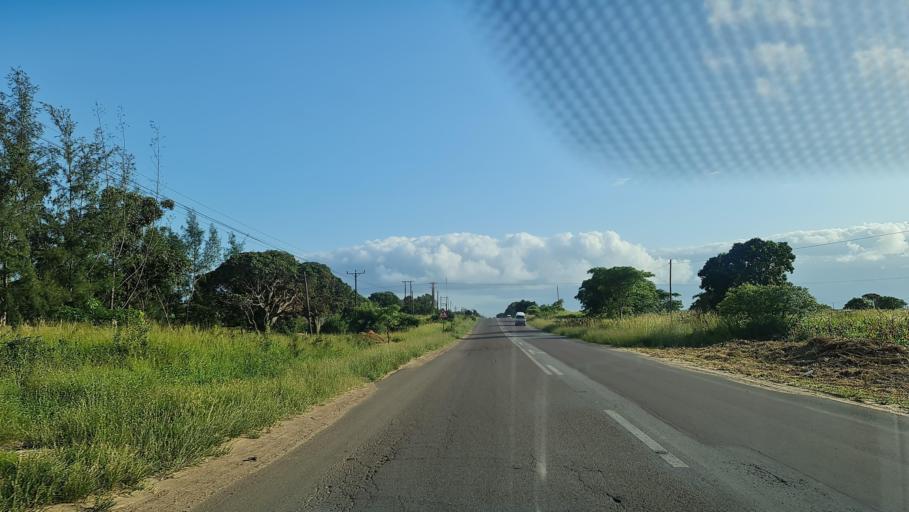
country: MZ
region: Maputo City
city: Maputo
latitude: -25.6776
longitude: 32.6671
